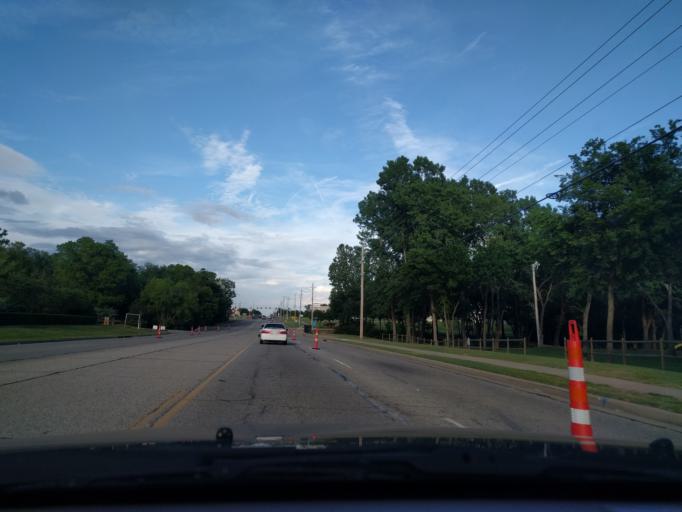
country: US
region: Oklahoma
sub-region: Tulsa County
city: Broken Arrow
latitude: 36.0608
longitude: -95.8370
